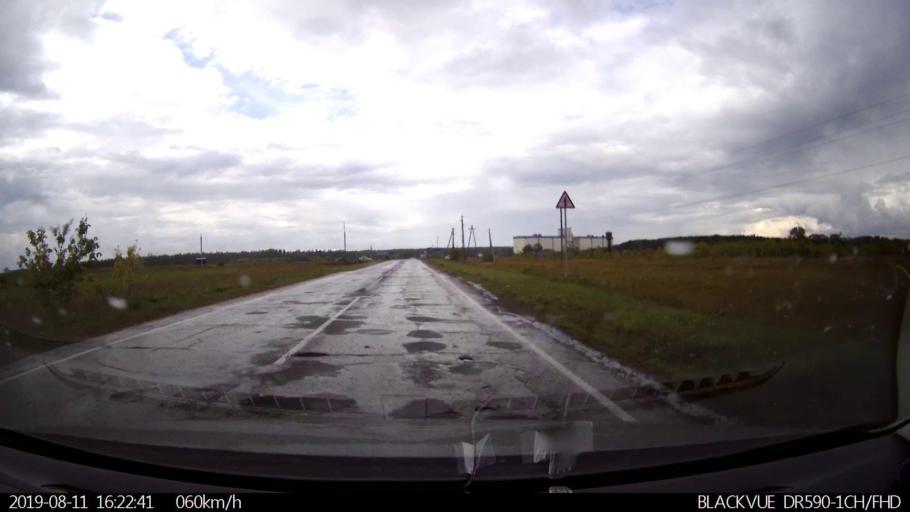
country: RU
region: Ulyanovsk
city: Mayna
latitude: 54.0901
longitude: 47.5916
